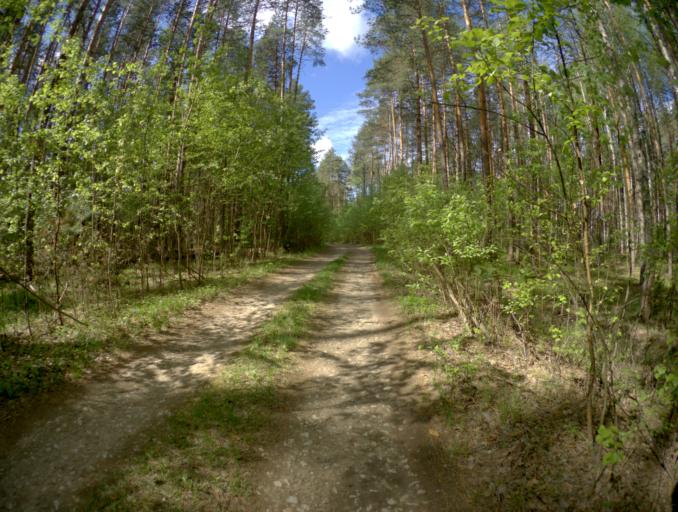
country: RU
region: Rjazan
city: Spas-Klepiki
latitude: 55.2420
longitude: 40.0644
